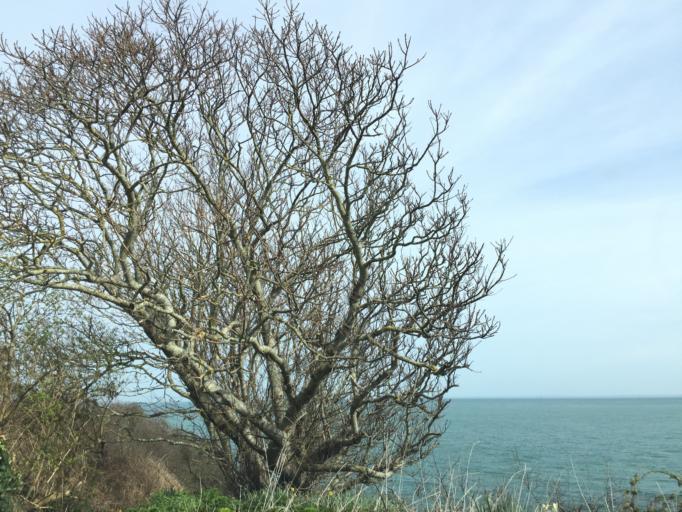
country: JE
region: St Helier
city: Saint Helier
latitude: 49.2325
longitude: -2.0248
